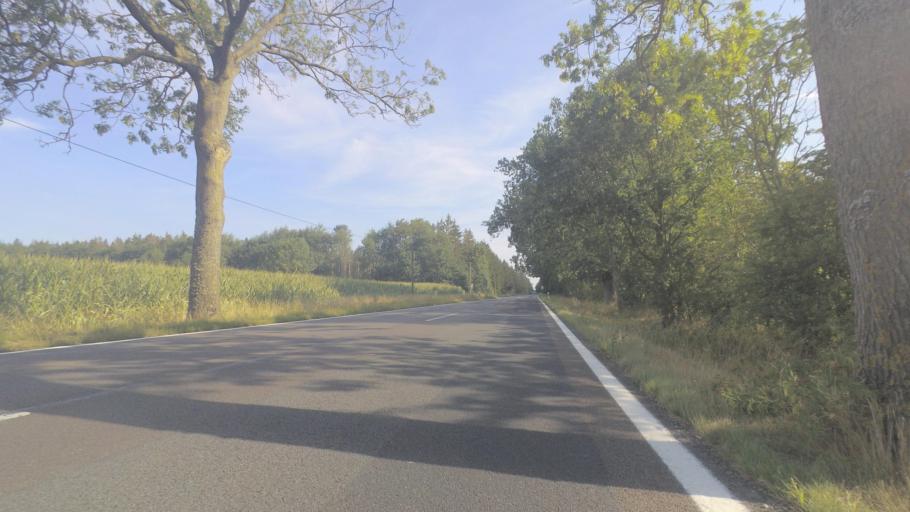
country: DE
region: Mecklenburg-Vorpommern
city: Grimmen
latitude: 54.0436
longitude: 13.1225
